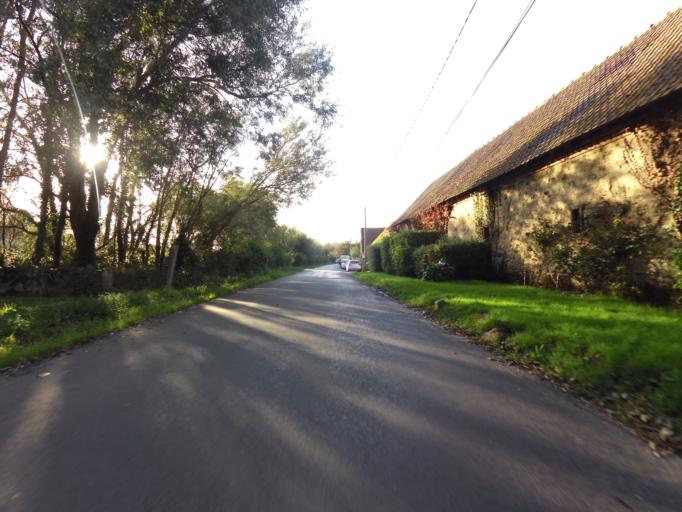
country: FR
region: Nord-Pas-de-Calais
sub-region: Departement du Pas-de-Calais
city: Wimille
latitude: 50.7484
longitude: 1.6200
